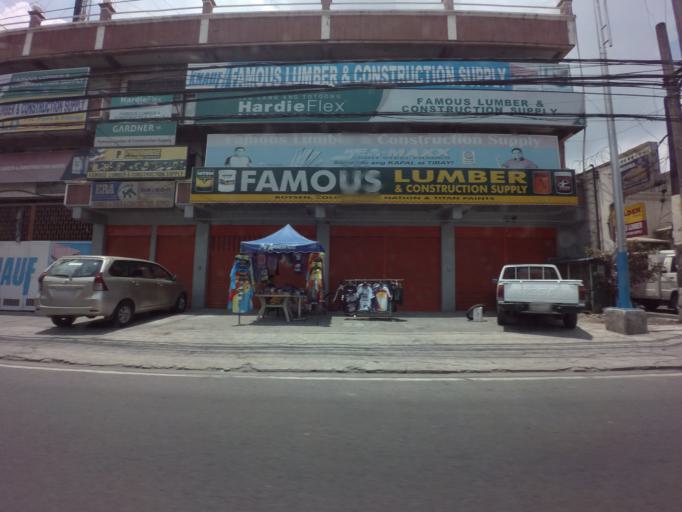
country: PH
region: Calabarzon
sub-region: Province of Laguna
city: San Pedro
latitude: 14.4062
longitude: 121.0468
